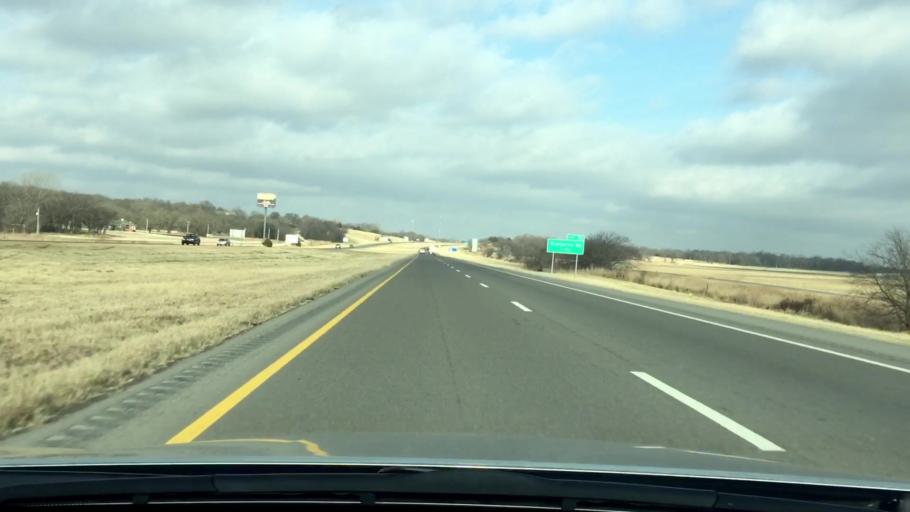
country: US
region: Oklahoma
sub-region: Garvin County
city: Pauls Valley
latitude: 34.7454
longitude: -97.2686
